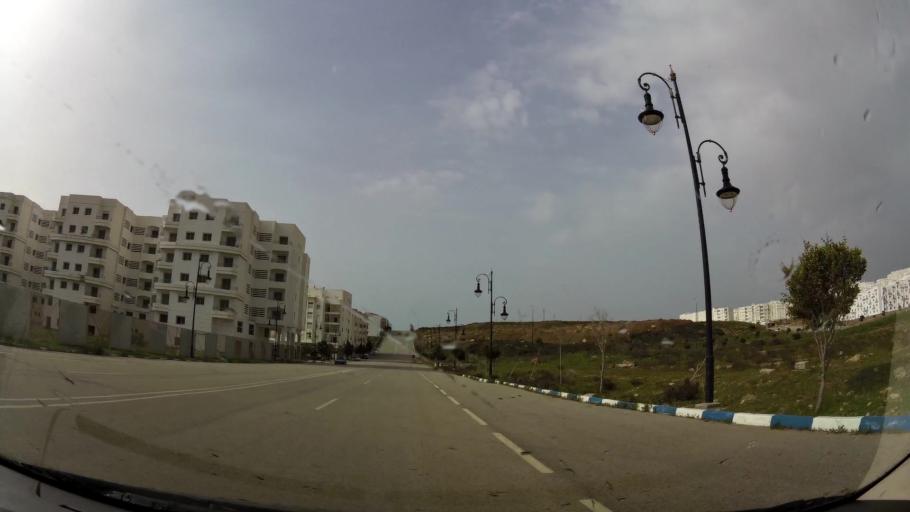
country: MA
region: Tanger-Tetouan
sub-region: Tanger-Assilah
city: Boukhalef
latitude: 35.7022
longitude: -5.9350
